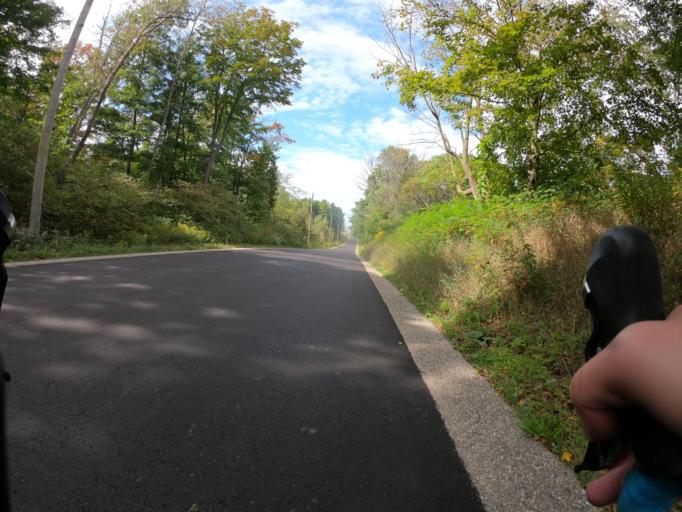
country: CA
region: Ontario
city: Kitchener
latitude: 43.3764
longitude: -80.6175
